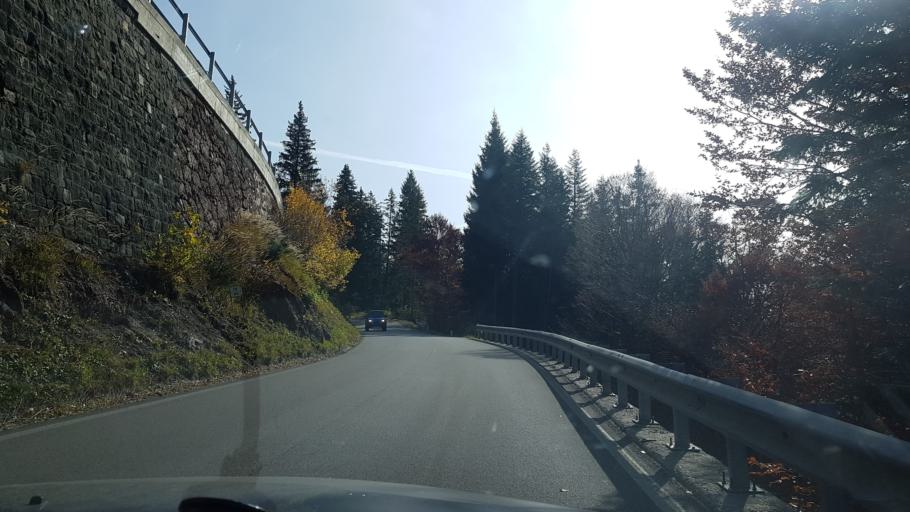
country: IT
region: Veneto
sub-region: Provincia di Belluno
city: Candide
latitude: 46.6465
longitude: 12.4508
